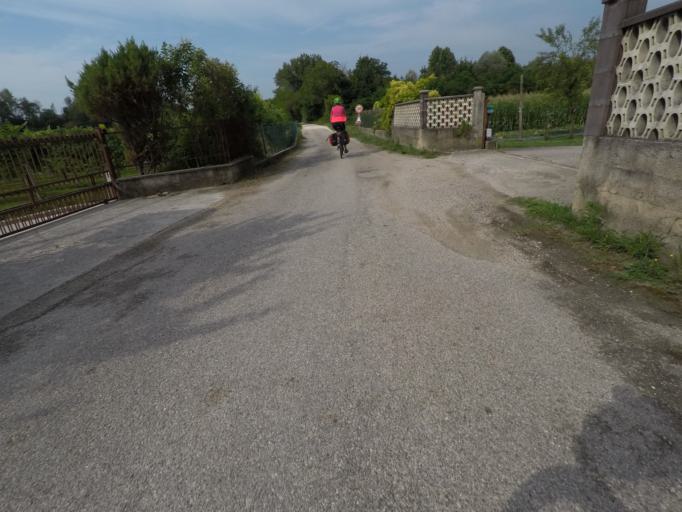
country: IT
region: Veneto
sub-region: Provincia di Treviso
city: Cappella Maggiore
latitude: 45.9706
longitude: 12.3372
